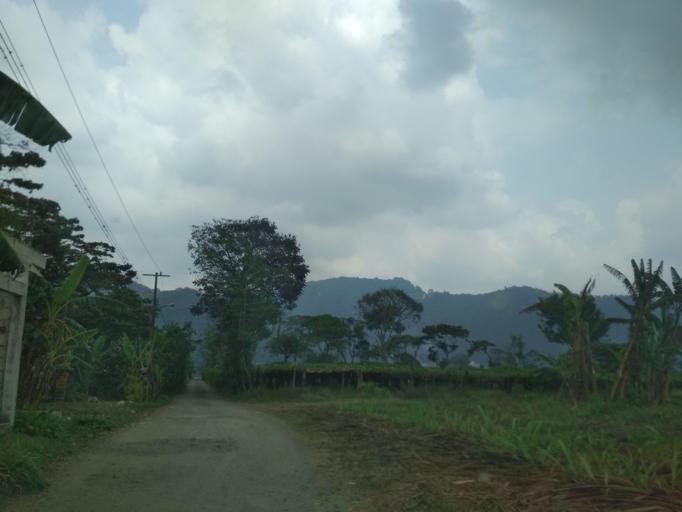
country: MX
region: Veracruz
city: Cuautlapan
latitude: 18.8665
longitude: -97.0173
